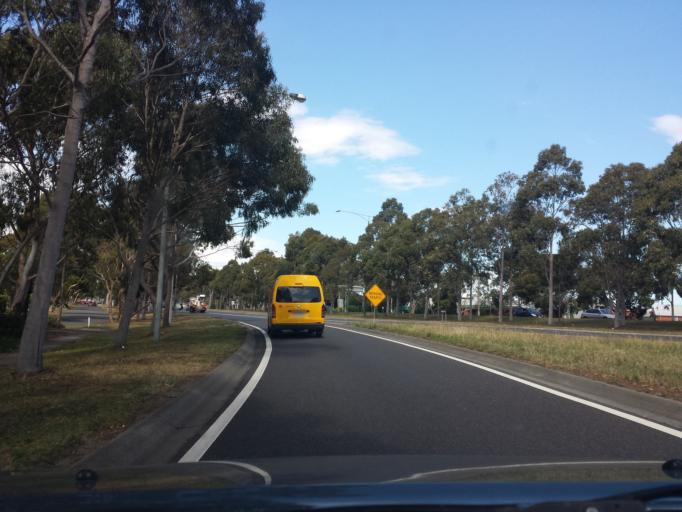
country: AU
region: Victoria
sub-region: Monash
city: Mulgrave
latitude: -37.9205
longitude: 145.1767
